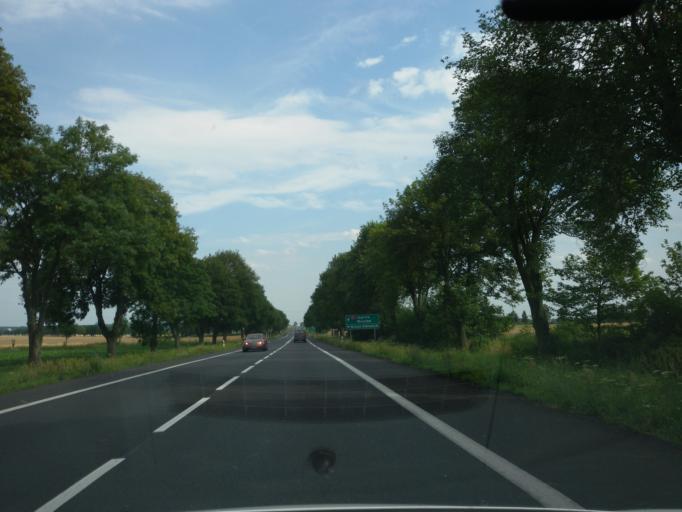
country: PL
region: Lower Silesian Voivodeship
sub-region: Powiat polkowicki
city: Gaworzyce
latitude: 51.6240
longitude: 15.9175
